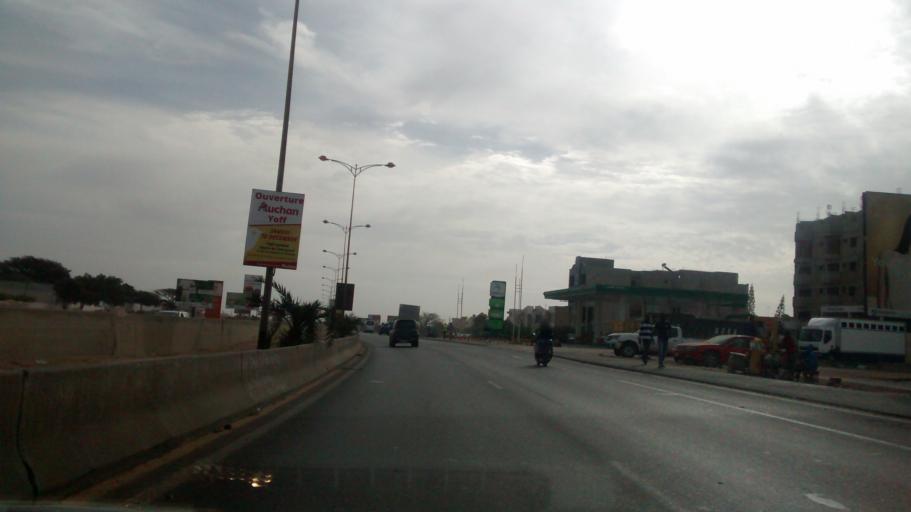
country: SN
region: Dakar
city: Grand Dakar
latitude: 14.7458
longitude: -17.4596
